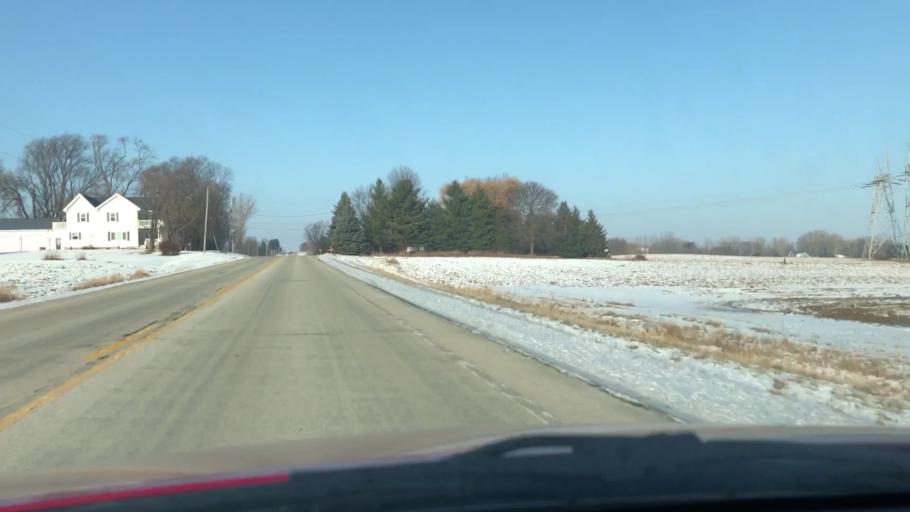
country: US
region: Wisconsin
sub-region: Outagamie County
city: Kimberly
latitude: 44.3676
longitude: -88.3748
